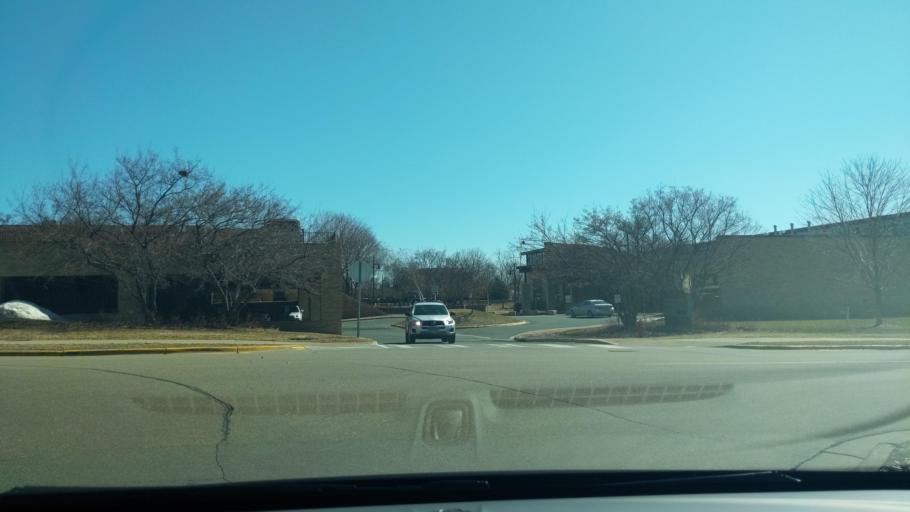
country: US
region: Minnesota
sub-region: Carver County
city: Chanhassen
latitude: 44.8632
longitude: -93.5403
